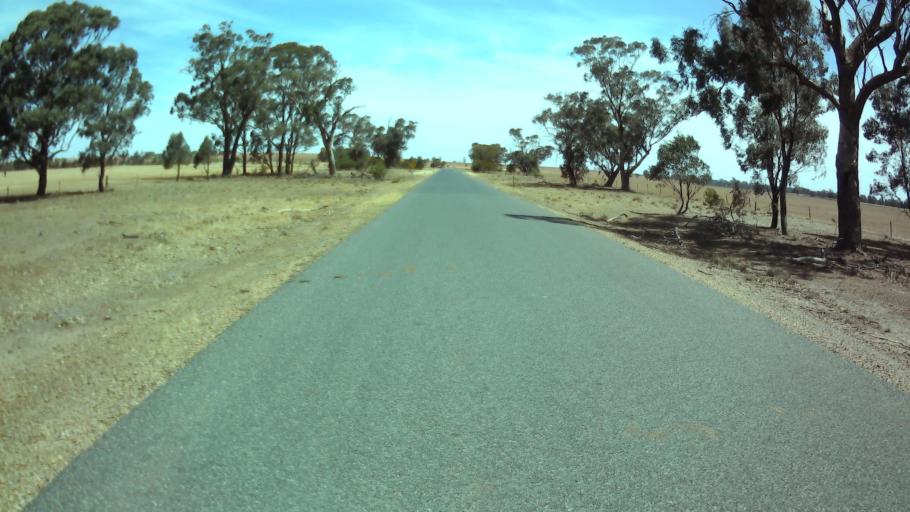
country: AU
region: New South Wales
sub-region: Weddin
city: Grenfell
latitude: -33.8841
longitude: 147.7423
